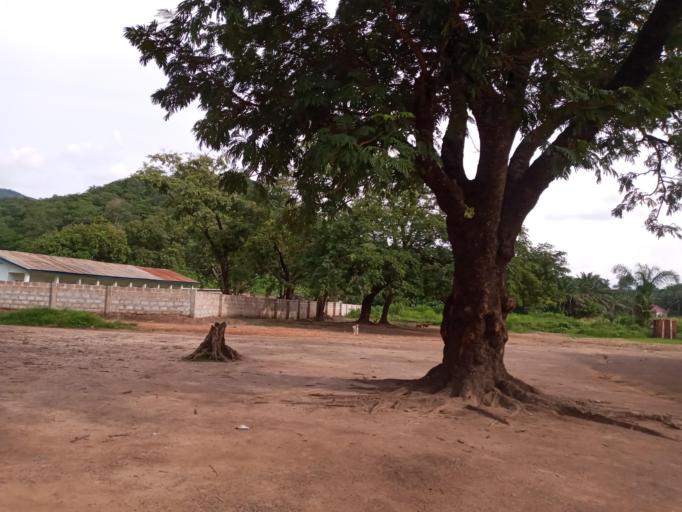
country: SL
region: Northern Province
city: Bumbuna
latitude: 9.0457
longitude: -11.7520
